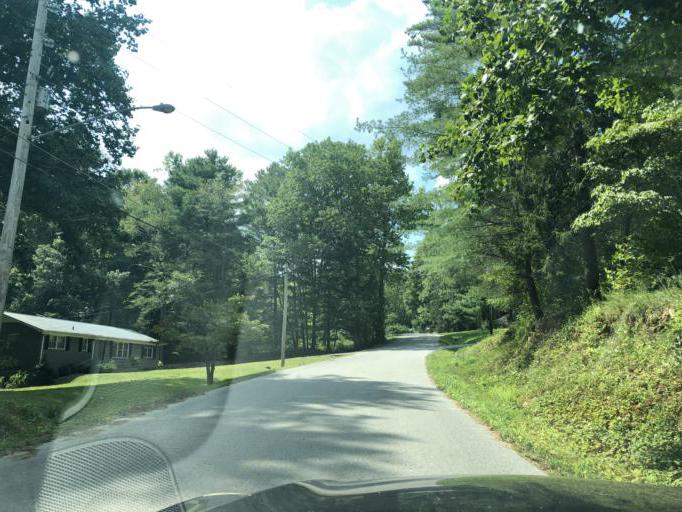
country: US
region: Tennessee
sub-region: Franklin County
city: Sewanee
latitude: 35.1941
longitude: -85.9202
